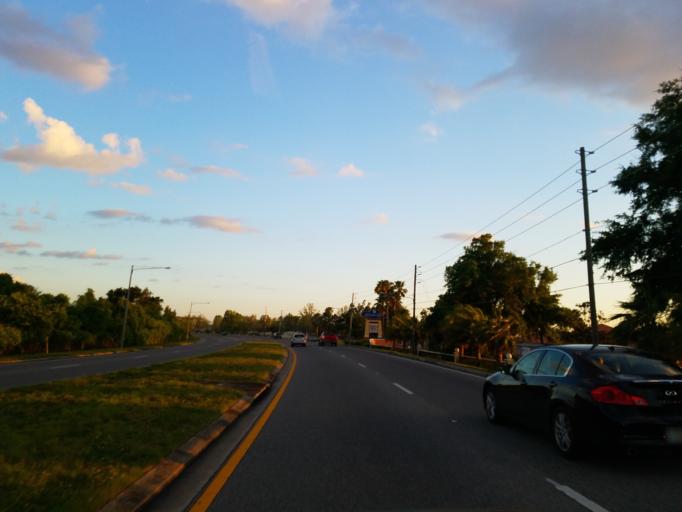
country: US
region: Florida
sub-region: Orange County
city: Doctor Phillips
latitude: 28.4218
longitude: -81.4760
